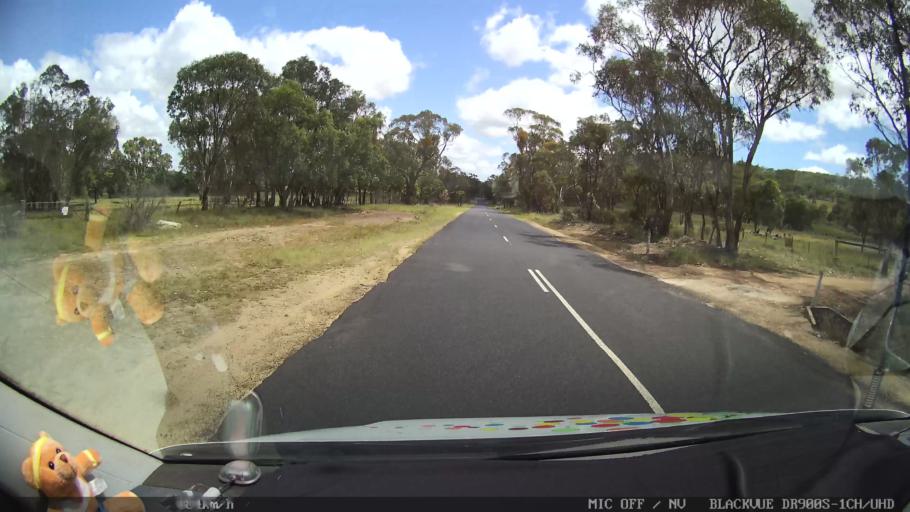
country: AU
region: New South Wales
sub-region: Glen Innes Severn
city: Glen Innes
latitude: -29.5376
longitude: 151.6731
